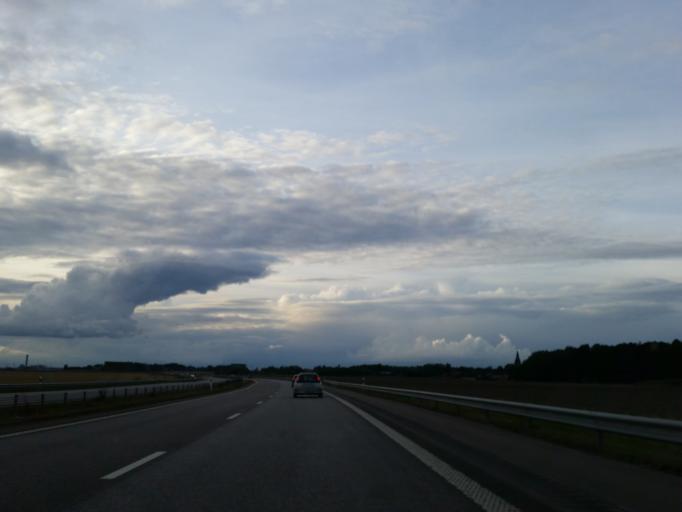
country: SE
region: Uppsala
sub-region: Uppsala Kommun
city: Saevja
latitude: 59.8212
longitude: 17.7508
